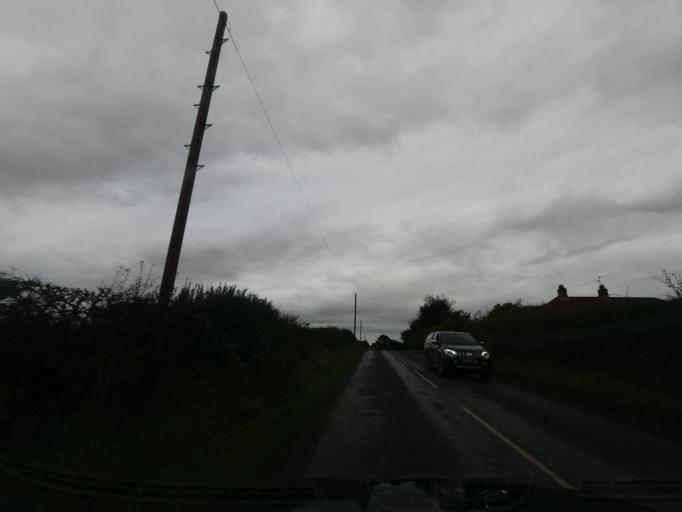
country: GB
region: England
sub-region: Northumberland
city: Ford
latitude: 55.6688
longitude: -2.1019
